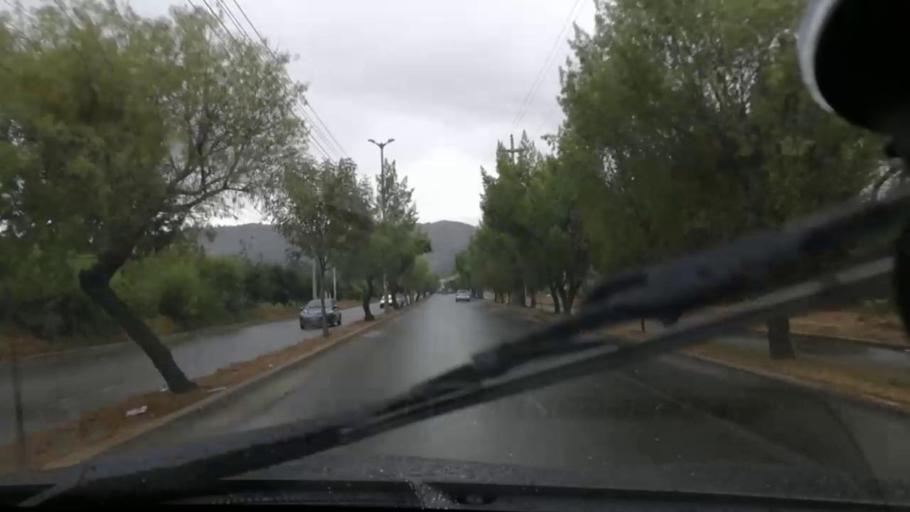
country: PE
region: Cajamarca
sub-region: Provincia de Cajamarca
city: Cajamarca
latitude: -7.1652
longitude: -78.4850
